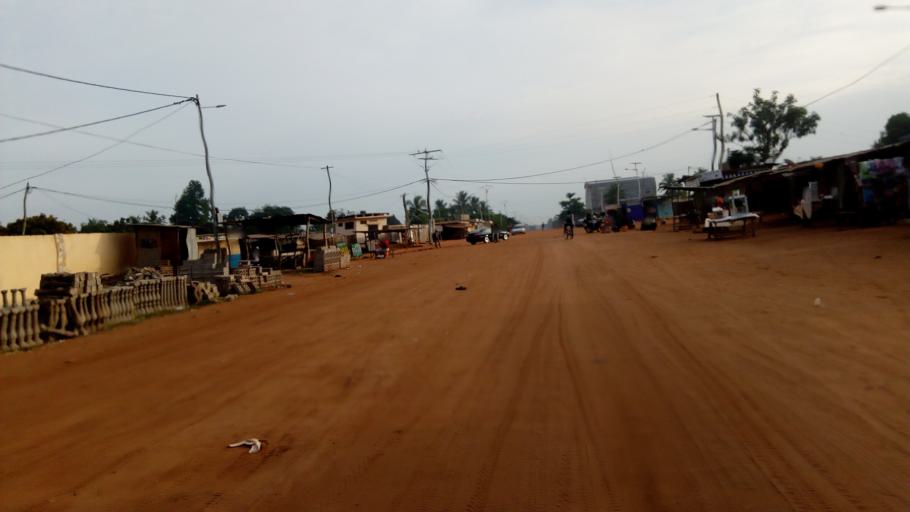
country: TG
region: Maritime
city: Lome
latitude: 6.1772
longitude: 1.1452
